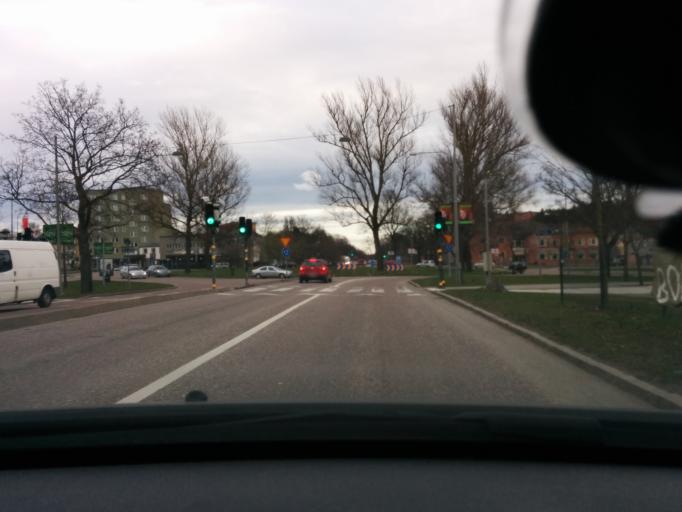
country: SE
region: Stockholm
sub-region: Stockholms Kommun
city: Bromma
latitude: 59.3400
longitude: 17.9379
